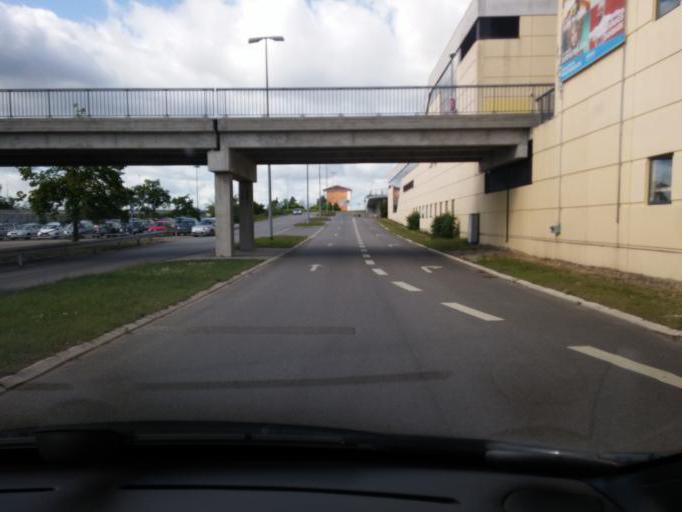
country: DK
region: Capital Region
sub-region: Ishoj Kommune
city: Ishoj
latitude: 55.5981
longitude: 12.3325
